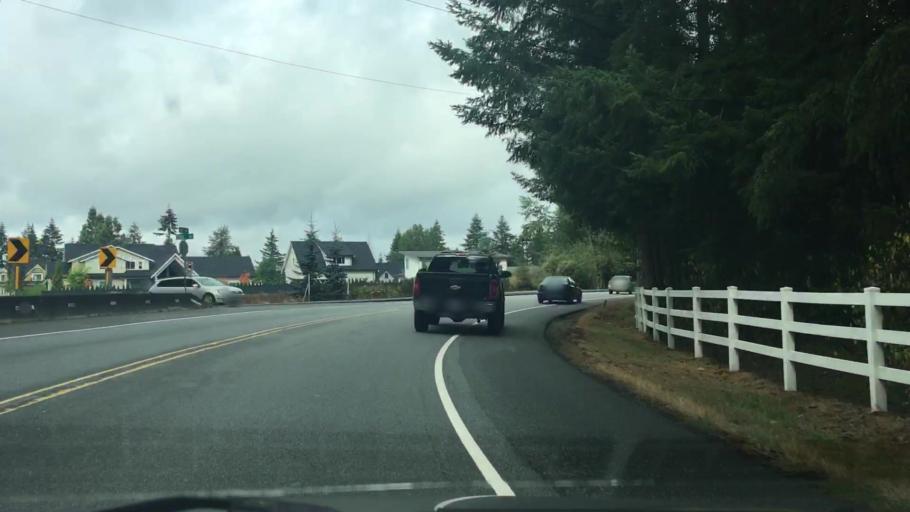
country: CA
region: British Columbia
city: Langley
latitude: 49.1042
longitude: -122.5638
